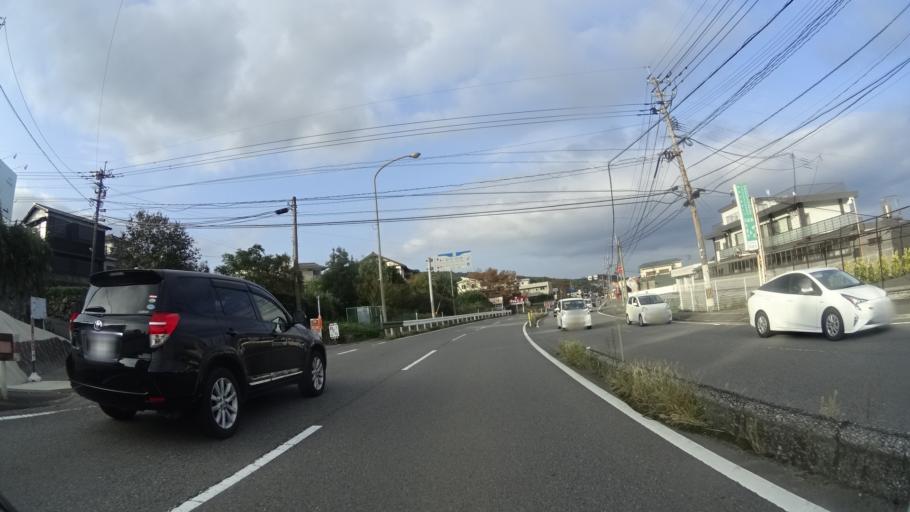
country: JP
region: Oita
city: Beppu
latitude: 33.3059
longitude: 131.4615
